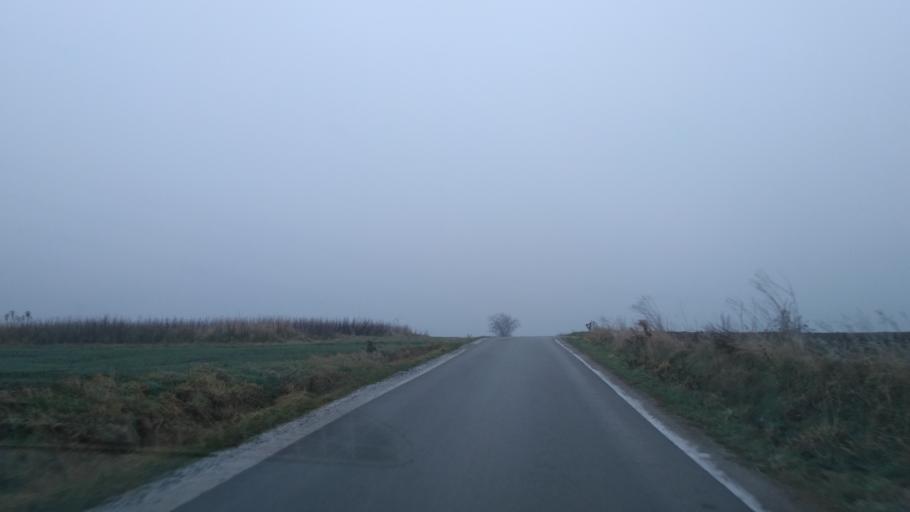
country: PL
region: Subcarpathian Voivodeship
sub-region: Powiat lancucki
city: Markowa
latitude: 50.0307
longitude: 22.3185
